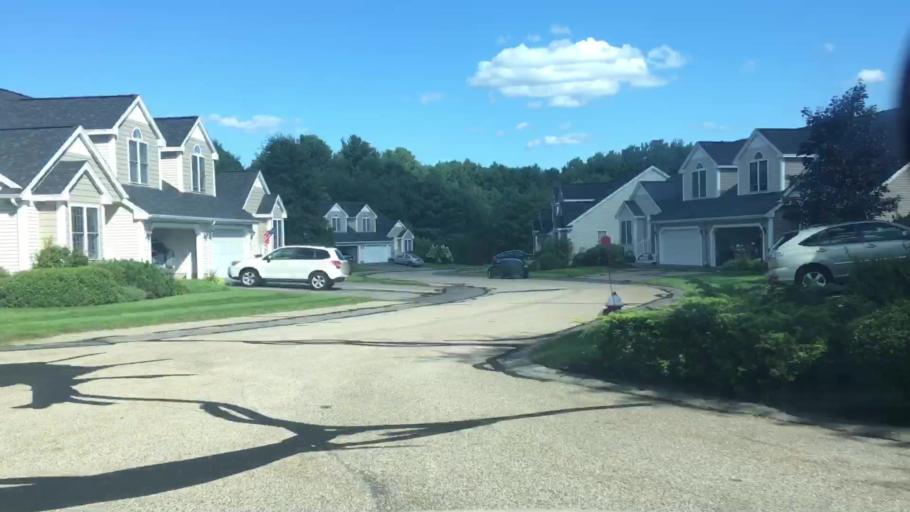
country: US
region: New Hampshire
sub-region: Strafford County
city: Dover
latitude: 43.1693
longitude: -70.8872
